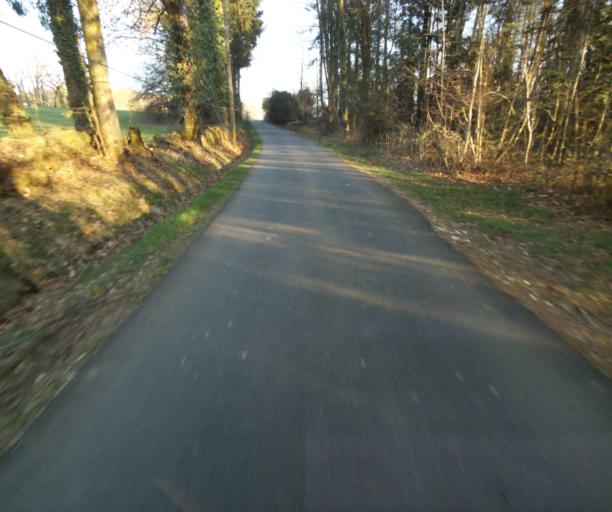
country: FR
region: Limousin
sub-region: Departement de la Correze
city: Seilhac
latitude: 45.3520
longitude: 1.7099
